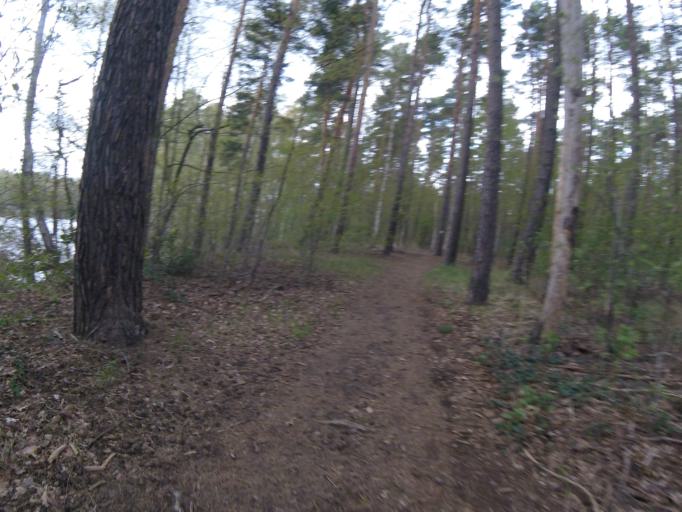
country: DE
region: Brandenburg
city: Bestensee
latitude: 52.2604
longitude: 13.6716
